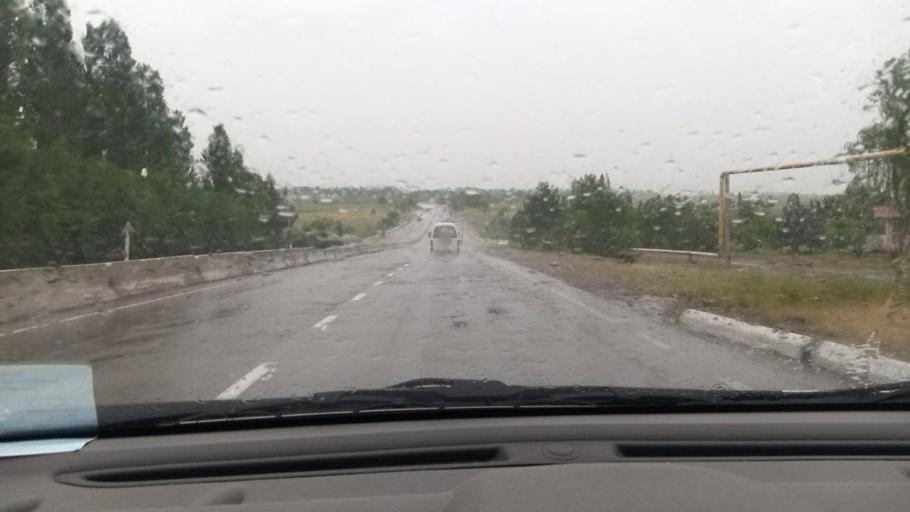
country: UZ
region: Toshkent
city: Angren
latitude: 40.9606
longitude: 69.9439
